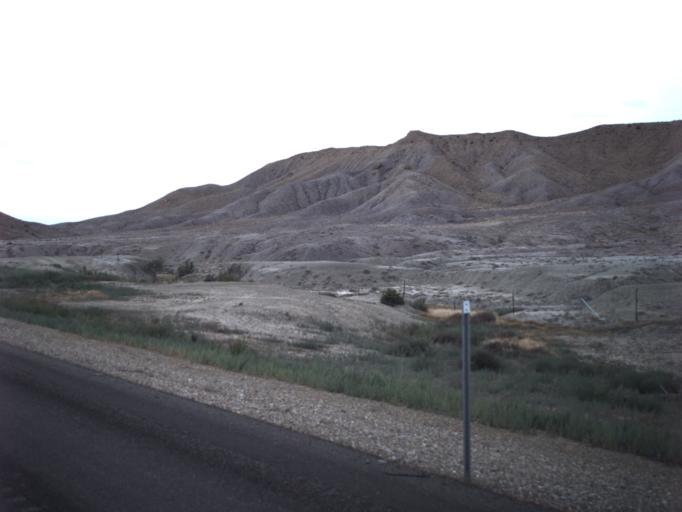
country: US
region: Utah
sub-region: Carbon County
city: East Carbon City
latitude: 39.2944
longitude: -110.3542
